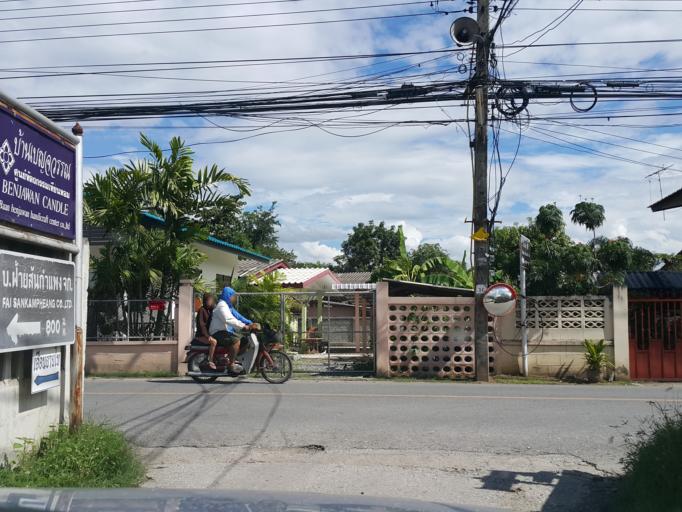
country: TH
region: Chiang Mai
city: San Kamphaeng
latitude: 18.7507
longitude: 99.1244
